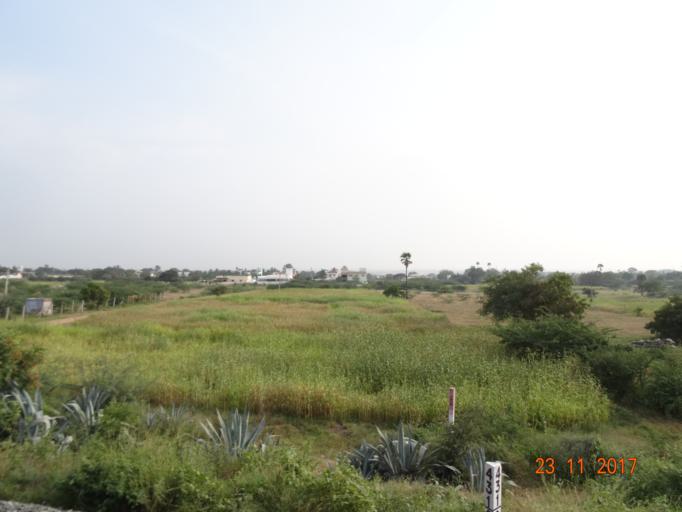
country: IN
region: Tamil Nadu
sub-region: Tiruppur
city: Uttukkuli
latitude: 11.1544
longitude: 77.4195
